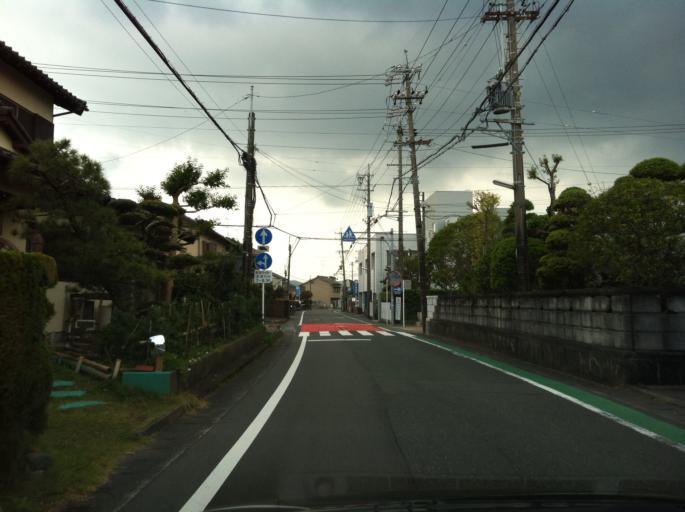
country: JP
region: Shizuoka
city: Kakegawa
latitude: 34.7786
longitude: 138.0351
